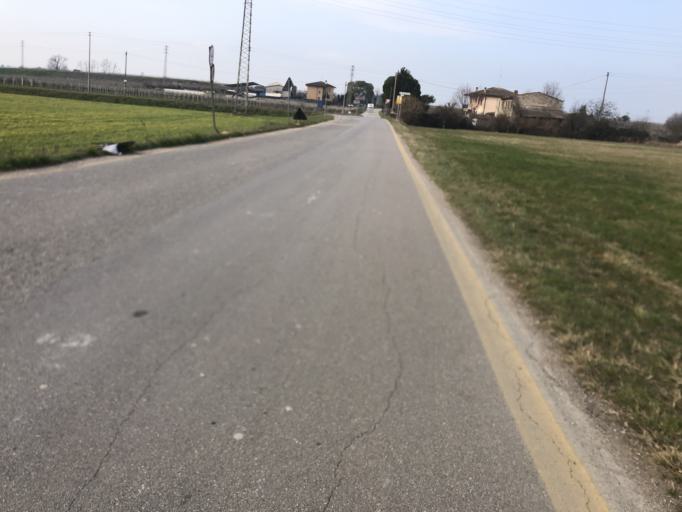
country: IT
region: Veneto
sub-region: Provincia di Verona
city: San Giorgio in Salici
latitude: 45.4129
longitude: 10.8019
